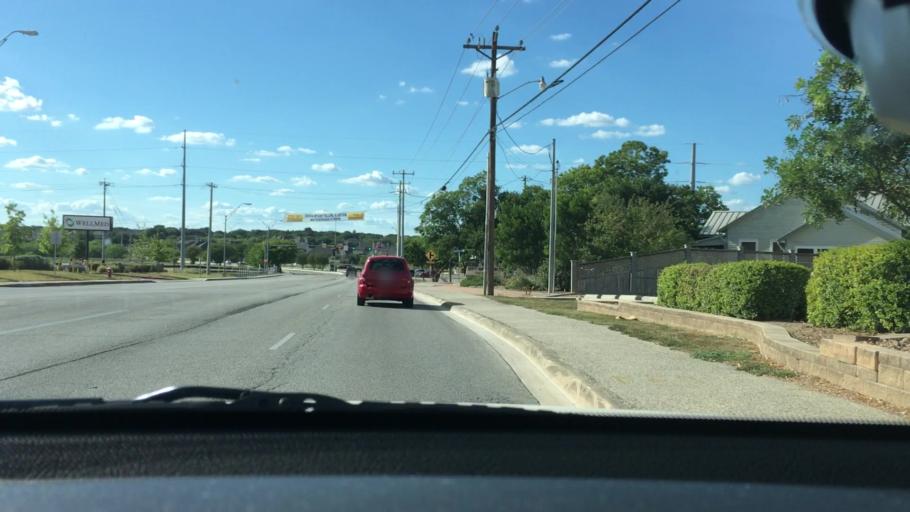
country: US
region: Texas
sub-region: Guadalupe County
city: Schertz
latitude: 29.5670
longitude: -98.2714
